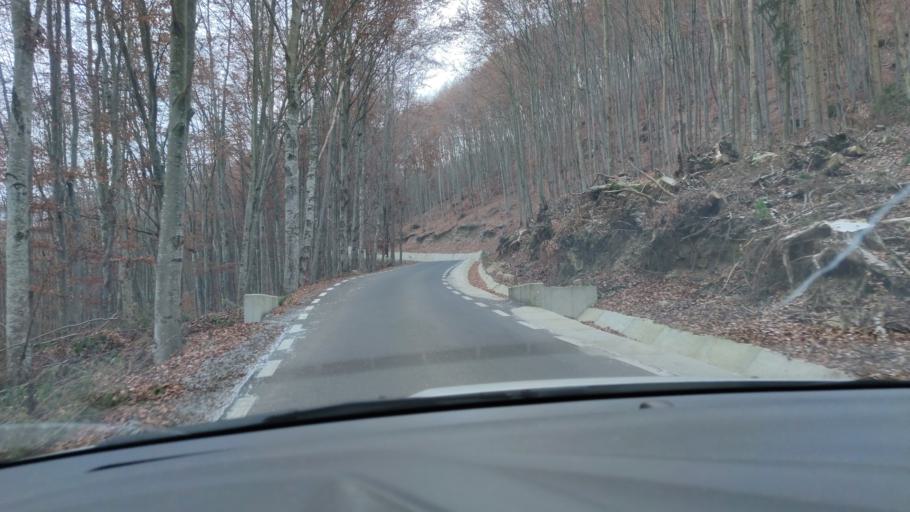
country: RO
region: Harghita
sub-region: Comuna Corund
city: Corund
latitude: 46.4823
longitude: 25.2271
